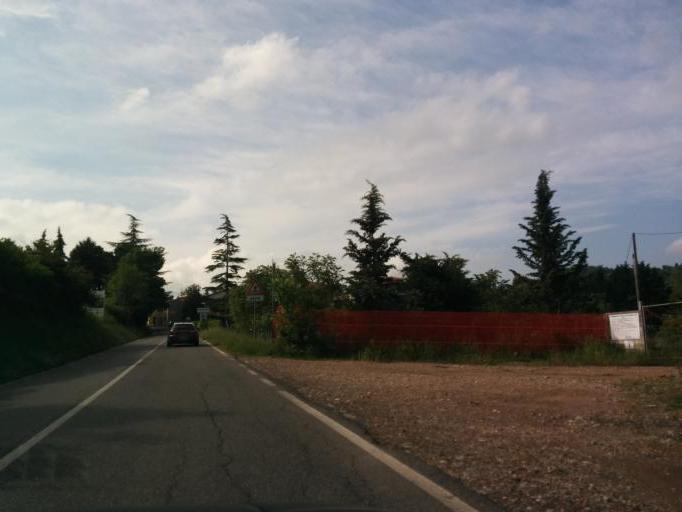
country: IT
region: Tuscany
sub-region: Province of Florence
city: San Casciano in Val di Pesa
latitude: 43.6185
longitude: 11.1888
